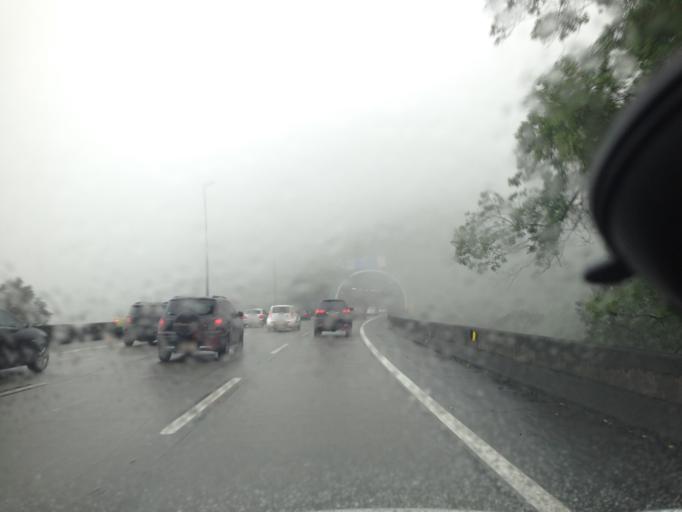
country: BR
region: Sao Paulo
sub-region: Cubatao
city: Cubatao
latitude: -23.8966
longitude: -46.5076
